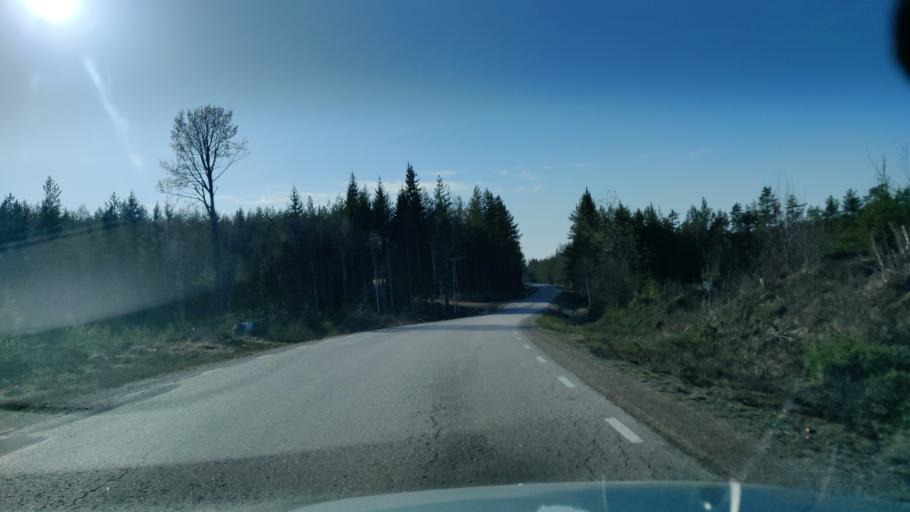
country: SE
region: Vaermland
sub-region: Hagfors Kommun
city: Ekshaerad
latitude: 59.9850
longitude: 13.3453
